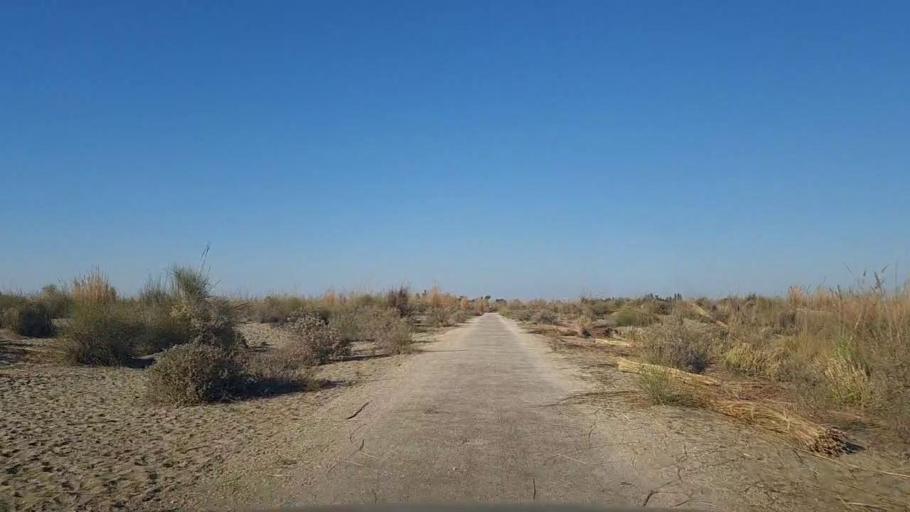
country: PK
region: Sindh
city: Khadro
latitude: 26.2481
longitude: 68.8643
